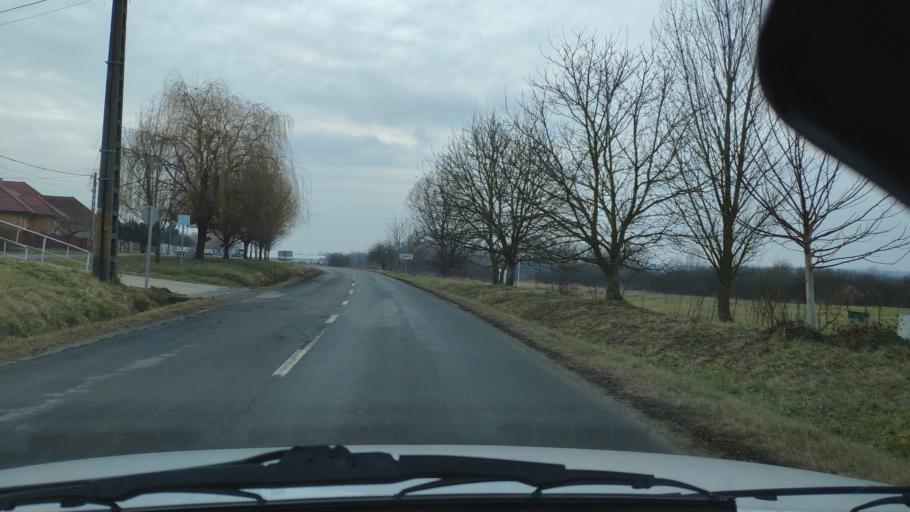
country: HU
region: Zala
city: Nagykanizsa
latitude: 46.5346
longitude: 16.9829
